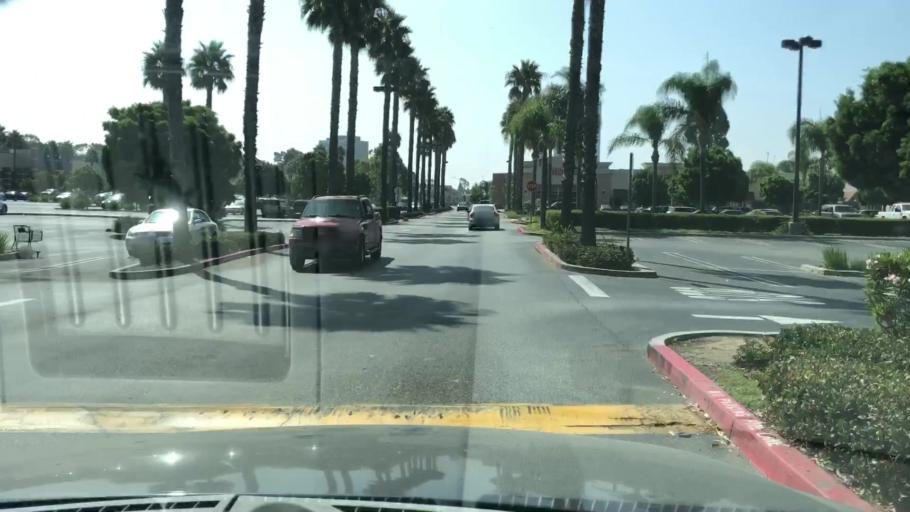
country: US
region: California
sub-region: Ventura County
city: El Rio
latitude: 34.2344
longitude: -119.1783
